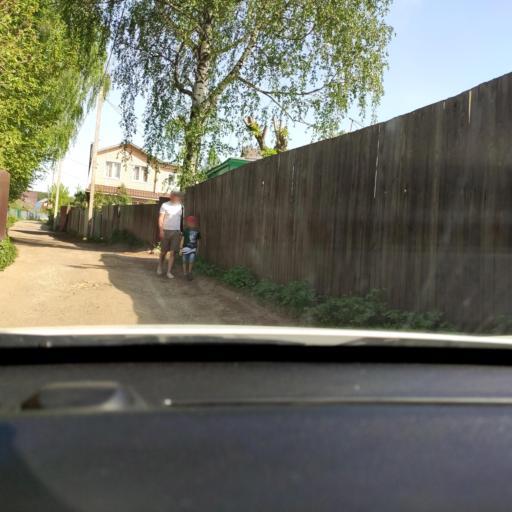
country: RU
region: Tatarstan
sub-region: Gorod Kazan'
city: Kazan
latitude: 55.8921
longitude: 49.0801
